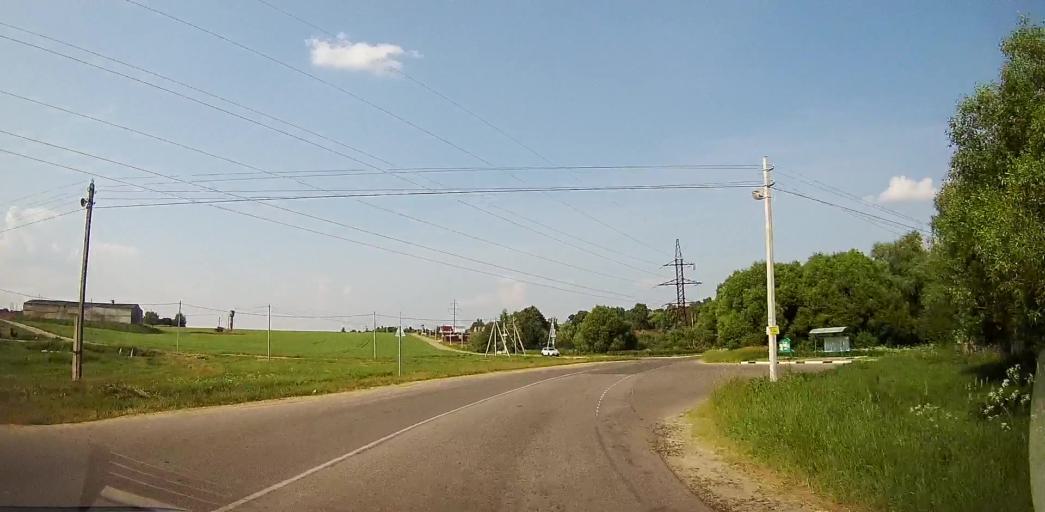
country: RU
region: Moskovskaya
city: Il'inskoye
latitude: 55.2938
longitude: 37.9427
